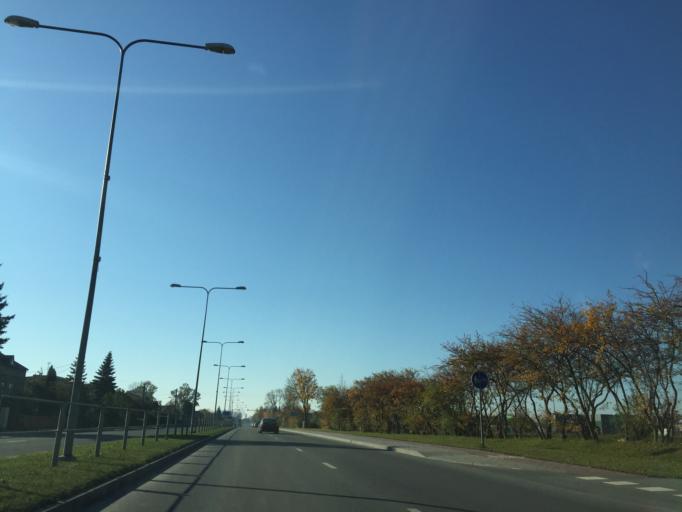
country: LT
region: Klaipedos apskritis
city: Kretinga
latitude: 55.8944
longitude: 21.2357
